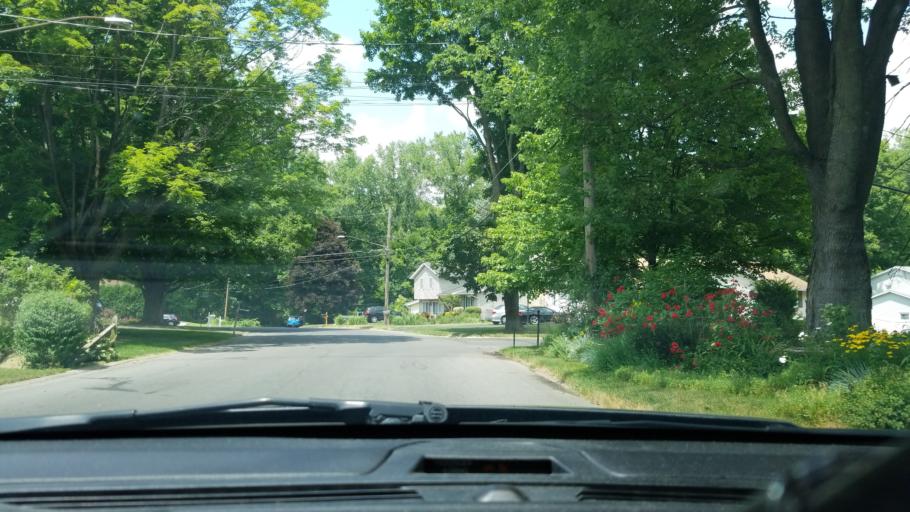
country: US
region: New York
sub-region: Onondaga County
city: Liverpool
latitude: 43.1453
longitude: -76.2261
